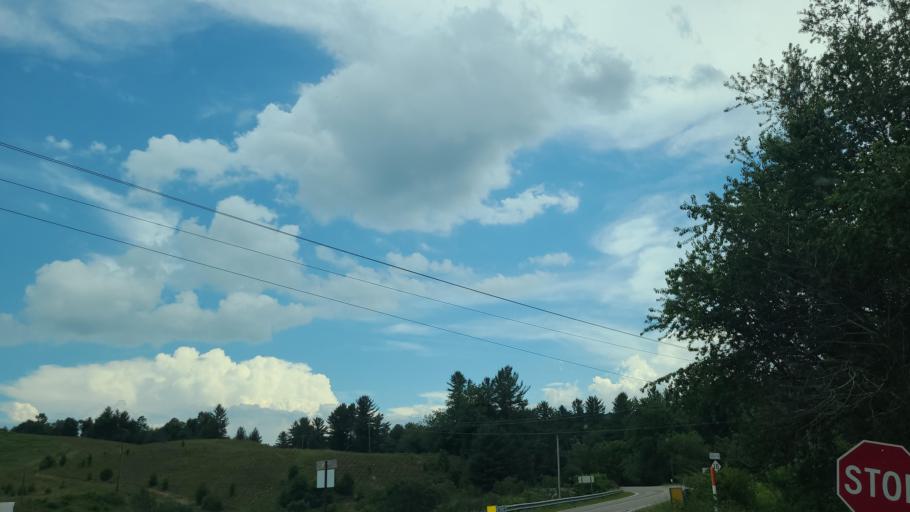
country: US
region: North Carolina
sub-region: Alleghany County
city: Sparta
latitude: 36.4124
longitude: -81.2639
